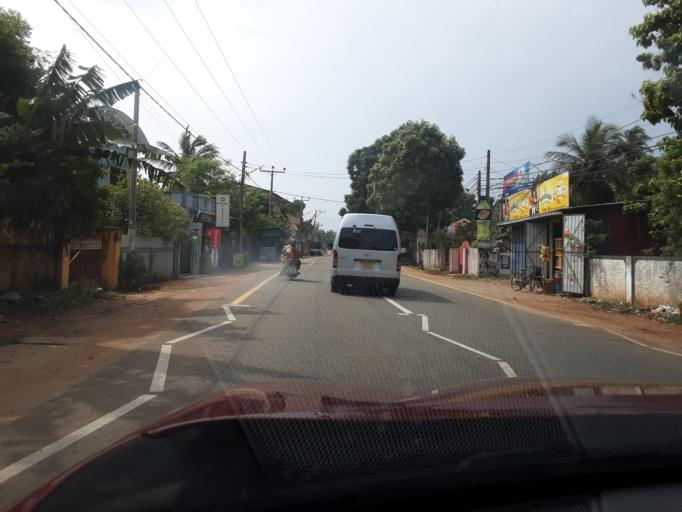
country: LK
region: Northern Province
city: Jaffna
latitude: 9.6607
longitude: 80.0457
